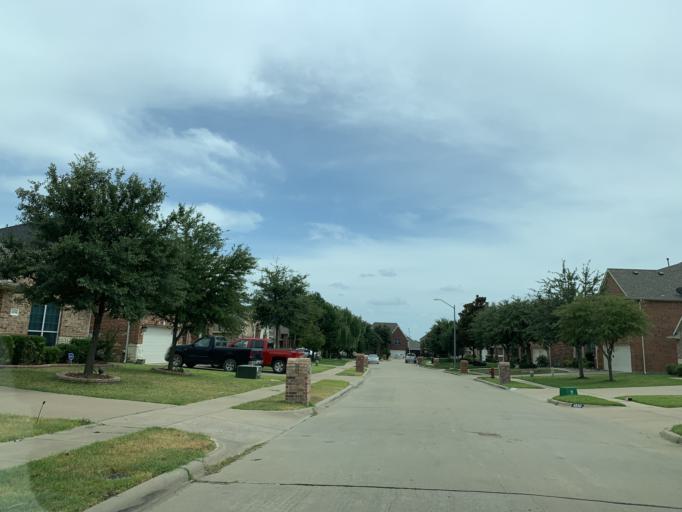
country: US
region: Texas
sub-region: Dallas County
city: Grand Prairie
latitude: 32.6526
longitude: -97.0401
